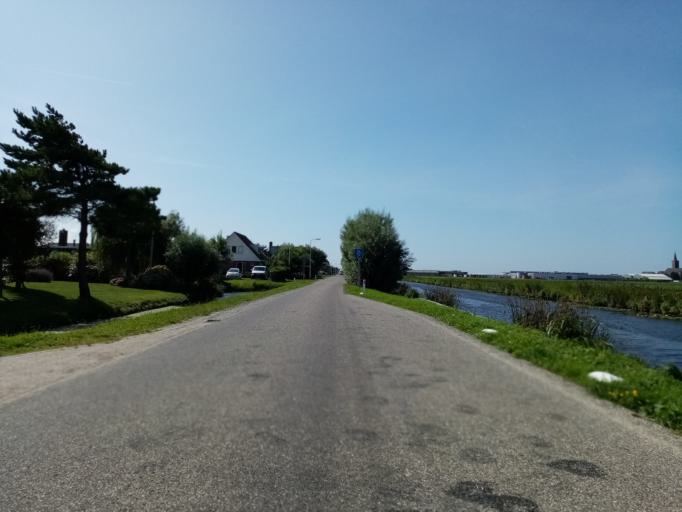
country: NL
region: South Holland
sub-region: Gemeente Hillegom
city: Hillegom
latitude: 52.3038
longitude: 4.5595
